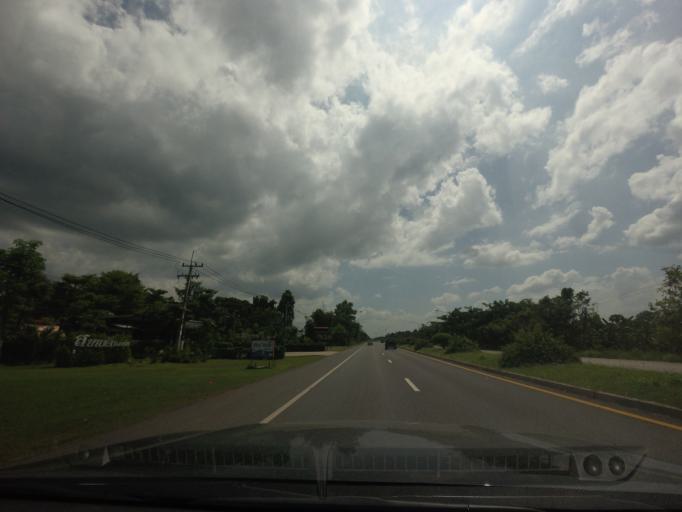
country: TH
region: Phetchabun
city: Nong Phai
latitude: 16.2013
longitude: 101.0890
